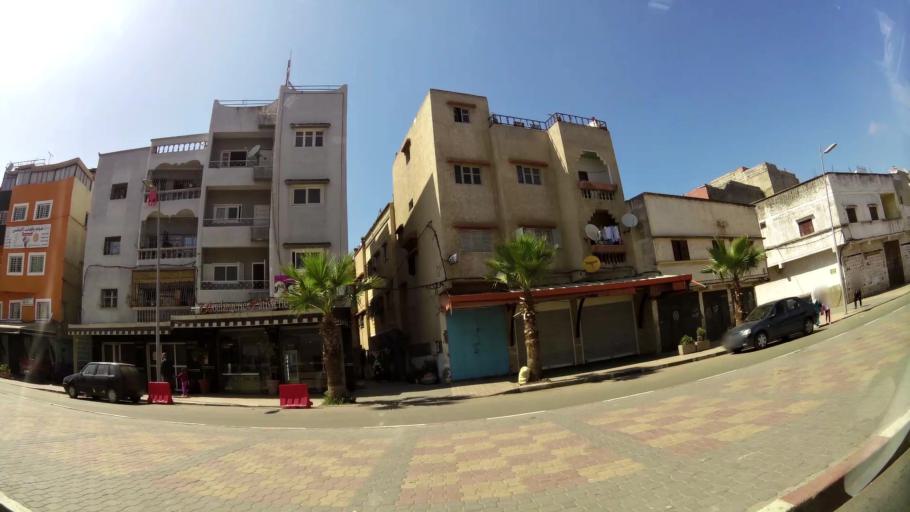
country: MA
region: Rabat-Sale-Zemmour-Zaer
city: Sale
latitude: 34.0638
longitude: -6.7697
